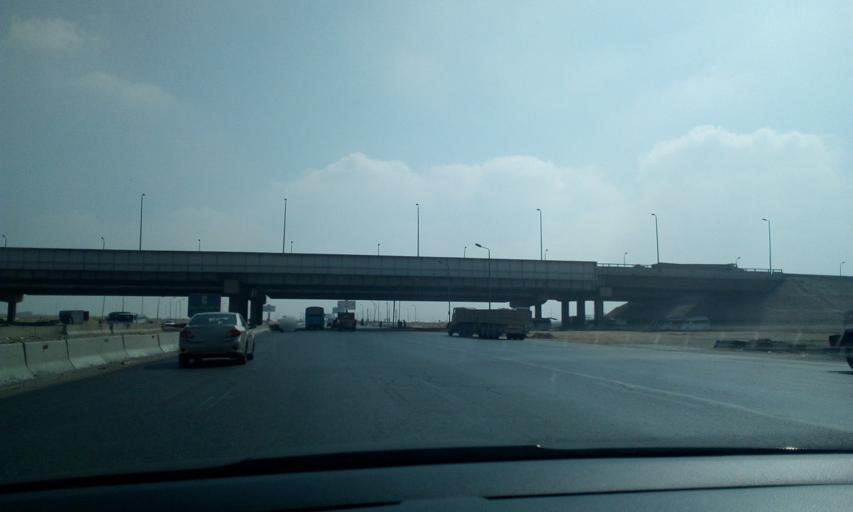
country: EG
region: Eastern Province
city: Bilbays
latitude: 30.2235
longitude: 31.6950
